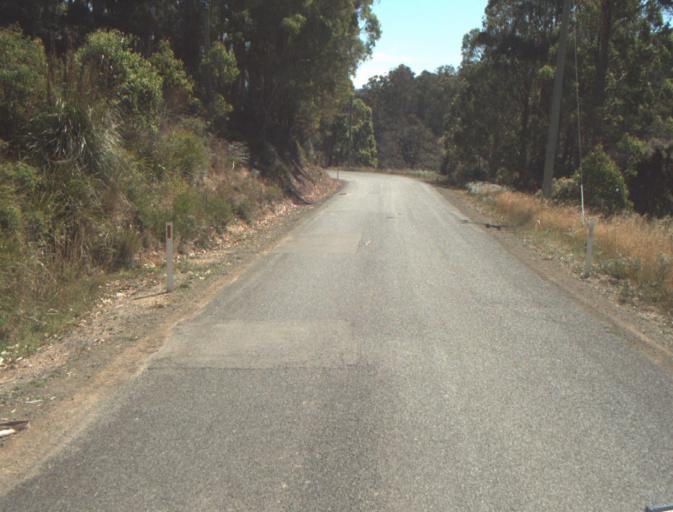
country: AU
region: Tasmania
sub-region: Dorset
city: Scottsdale
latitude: -41.3130
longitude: 147.3870
